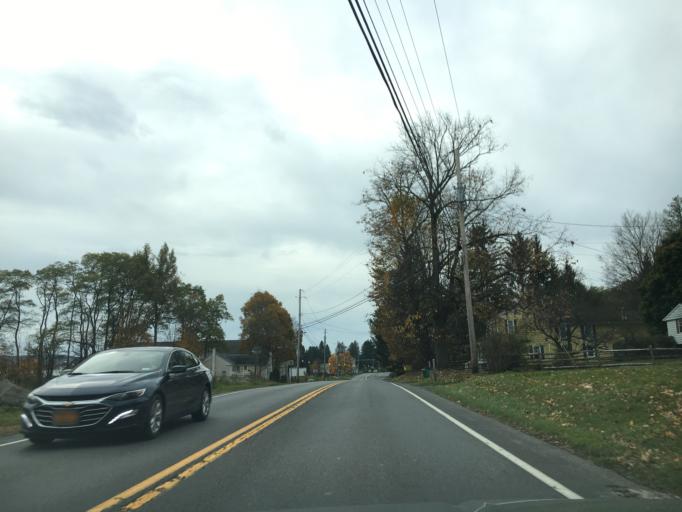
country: US
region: New York
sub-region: Otsego County
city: Cooperstown
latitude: 42.6526
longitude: -74.9644
